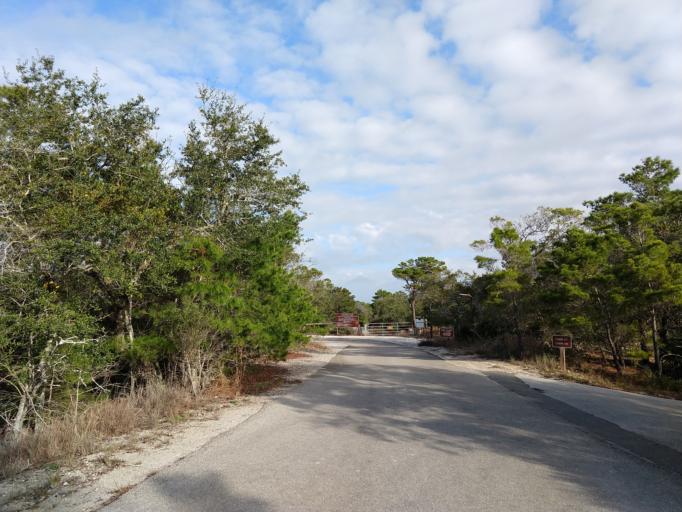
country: US
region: Florida
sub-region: Gulf County
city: Port Saint Joe
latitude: 29.7887
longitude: -85.4062
